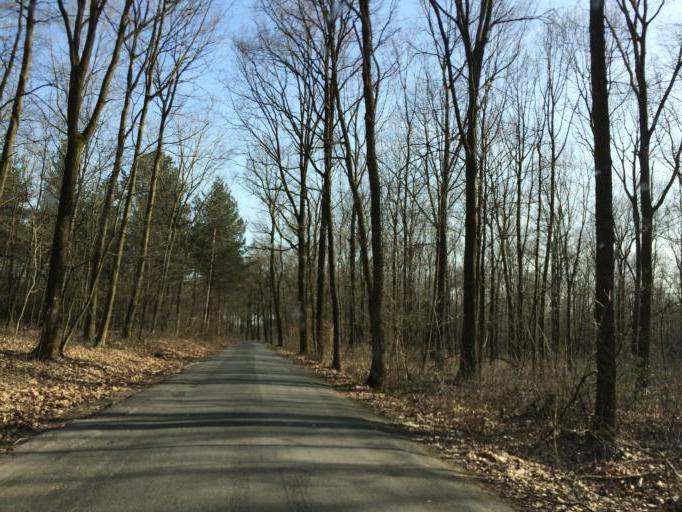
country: DE
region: North Rhine-Westphalia
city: Marl
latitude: 51.7026
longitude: 7.0295
